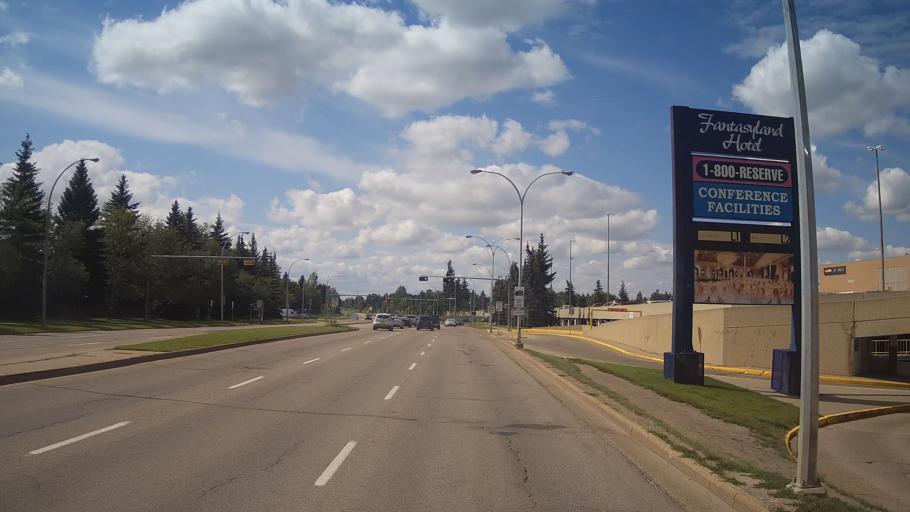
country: CA
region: Alberta
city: St. Albert
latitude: 53.5210
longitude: -113.6273
